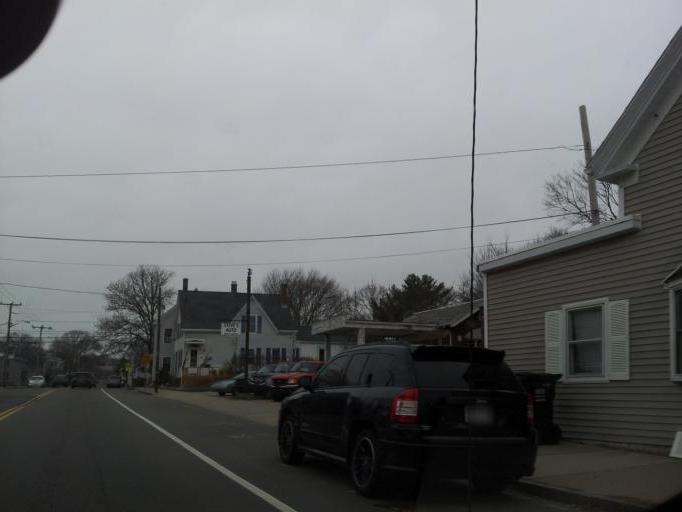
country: US
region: Massachusetts
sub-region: Plymouth County
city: Plymouth
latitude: 41.9524
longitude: -70.6577
